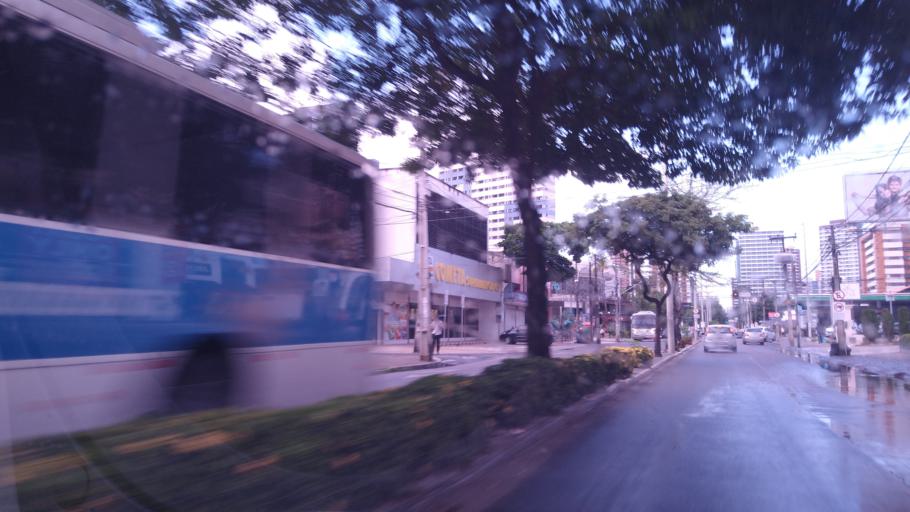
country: BR
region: Ceara
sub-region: Fortaleza
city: Fortaleza
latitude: -3.7341
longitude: -38.4923
